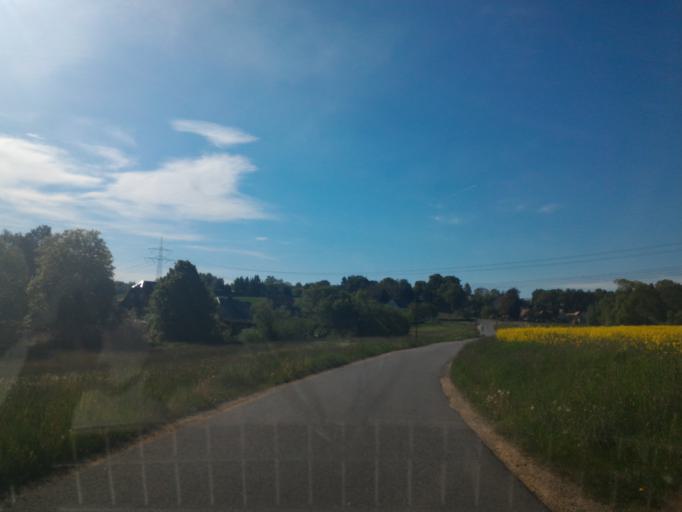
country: DE
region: Saxony
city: Niedercunnersdorf
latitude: 51.0431
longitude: 14.6642
